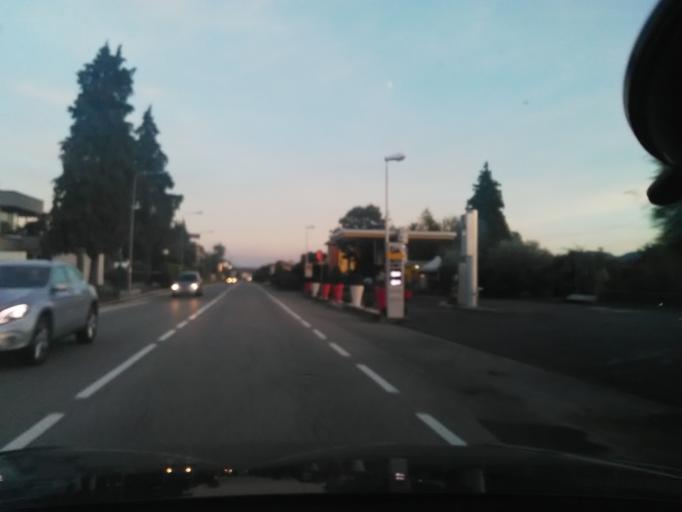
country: IT
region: Piedmont
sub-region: Provincia di Novara
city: Grignasco
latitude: 45.6743
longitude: 8.3450
